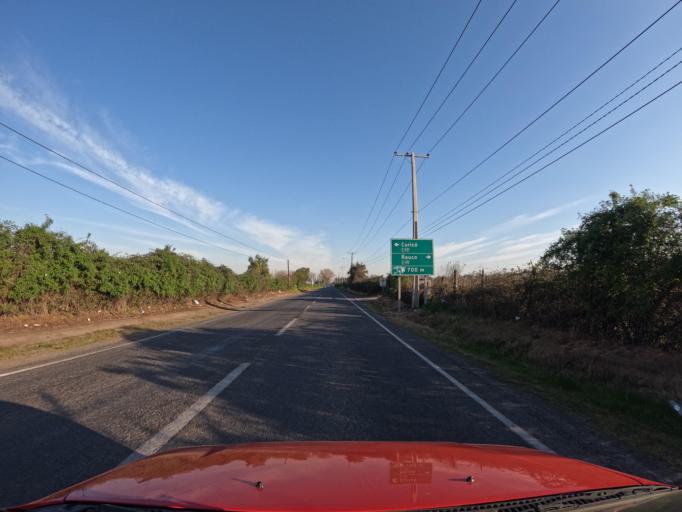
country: CL
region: Maule
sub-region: Provincia de Curico
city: Rauco
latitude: -34.9266
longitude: -71.2769
